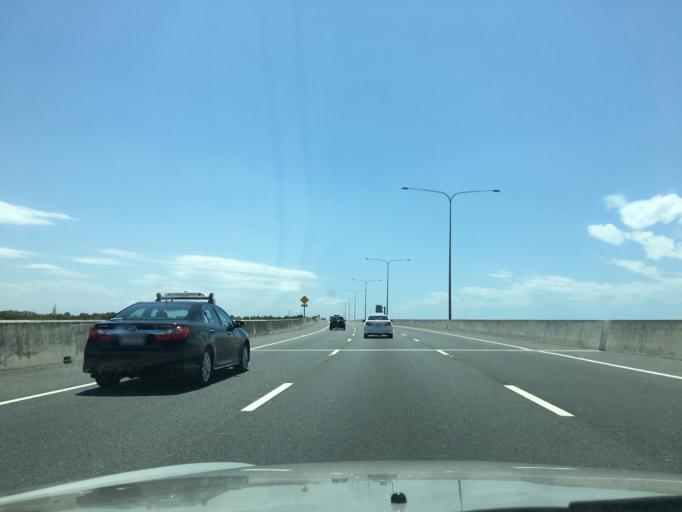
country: AU
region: Queensland
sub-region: Brisbane
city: Wavell Heights
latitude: -27.3994
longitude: 153.0939
